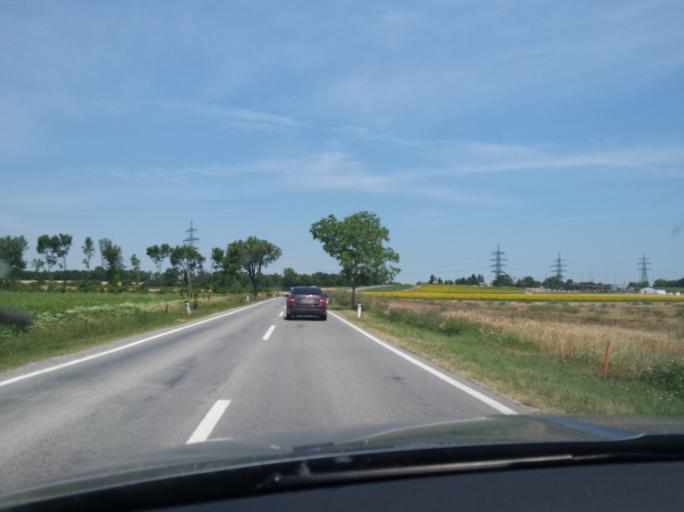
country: AT
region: Lower Austria
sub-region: Politischer Bezirk Bruck an der Leitha
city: Rohrau
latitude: 48.0912
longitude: 16.8622
